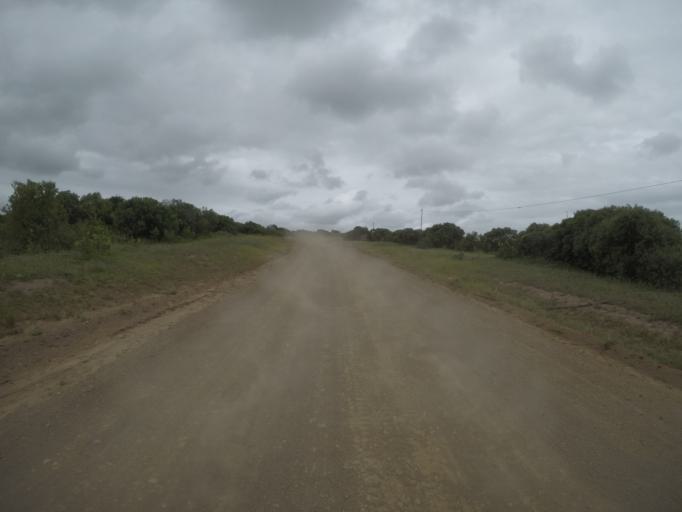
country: ZA
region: KwaZulu-Natal
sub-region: uThungulu District Municipality
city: Empangeni
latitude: -28.5988
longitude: 31.8382
